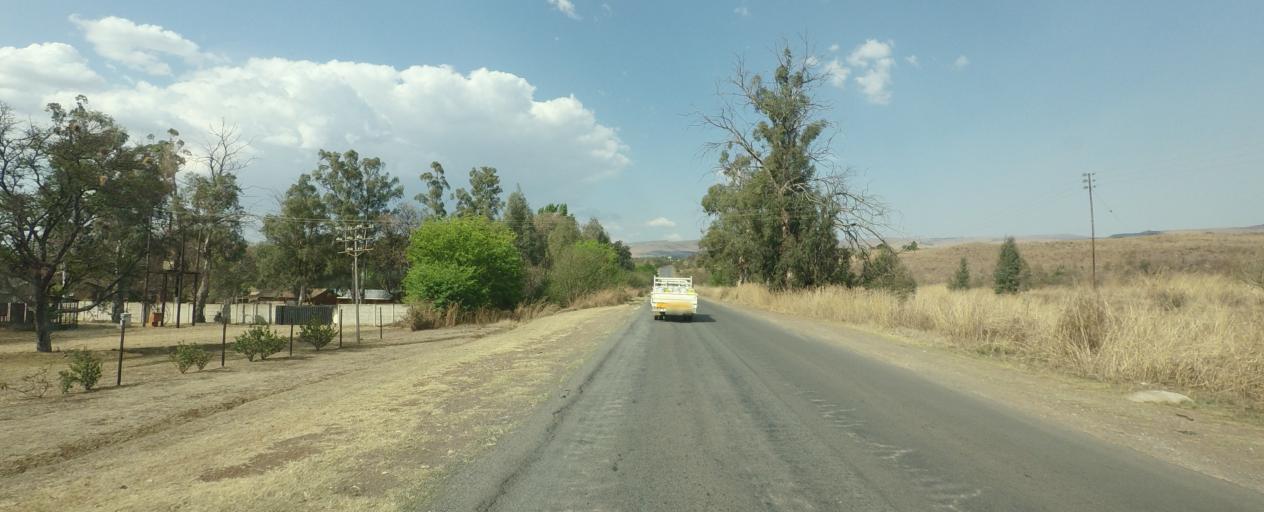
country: ZA
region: Mpumalanga
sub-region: Ehlanzeni District
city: Lydenburg
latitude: -25.1165
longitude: 30.4379
